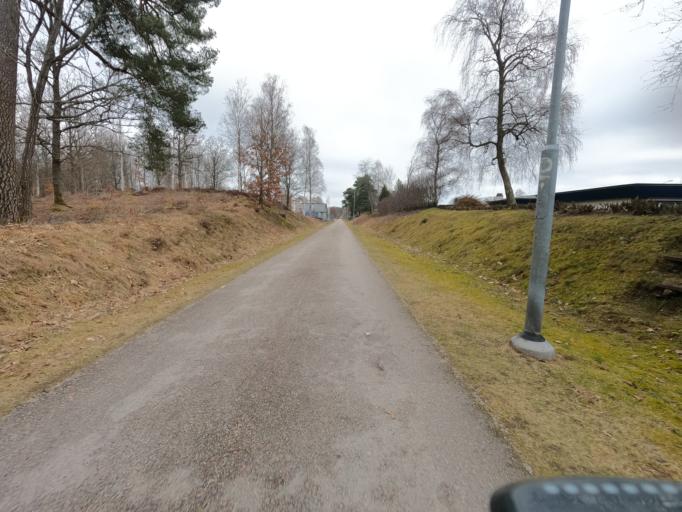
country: SE
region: Kronoberg
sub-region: Ljungby Kommun
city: Ljungby
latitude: 56.8349
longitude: 13.9573
